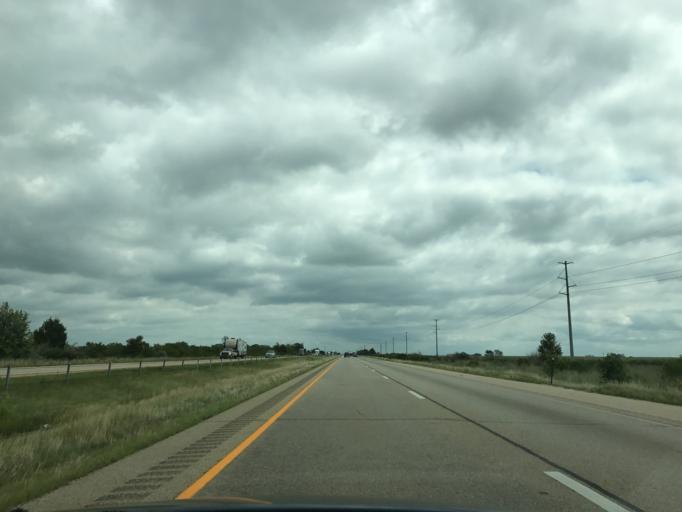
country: US
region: Illinois
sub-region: LaSalle County
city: Deer Park
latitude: 41.3679
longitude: -88.9608
